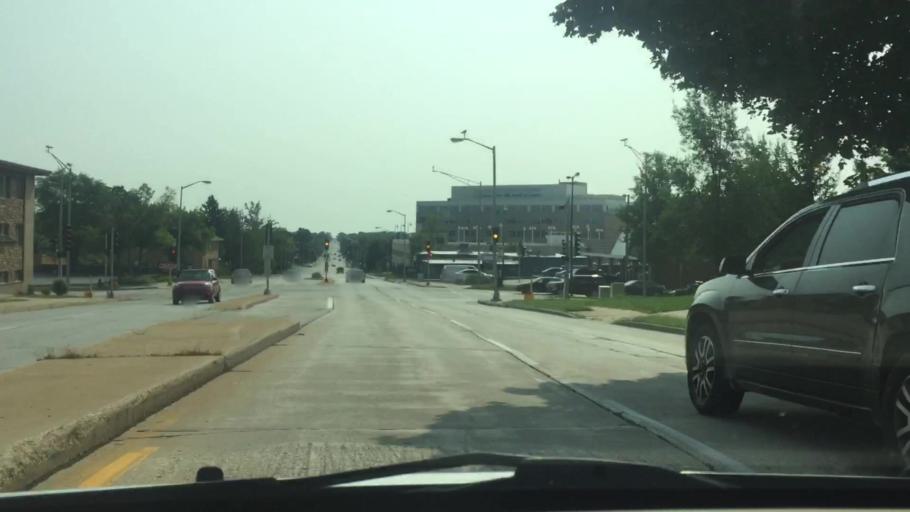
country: US
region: Wisconsin
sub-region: Milwaukee County
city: West Allis
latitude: 43.0026
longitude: -88.0280
